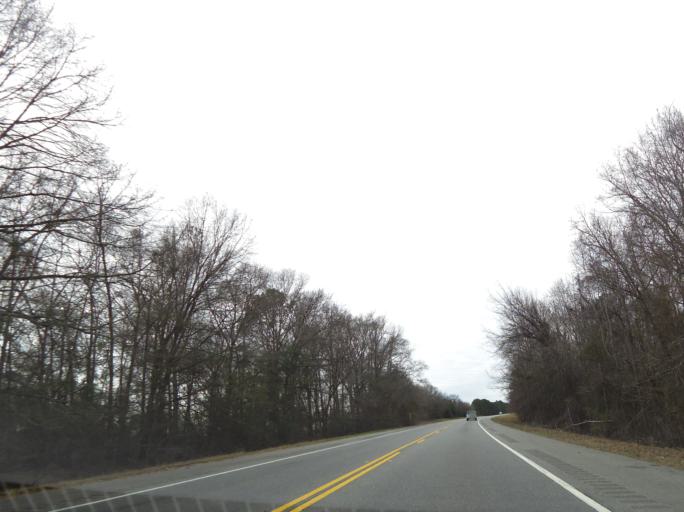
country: US
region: Georgia
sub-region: Bibb County
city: West Point
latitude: 32.7972
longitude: -83.7683
